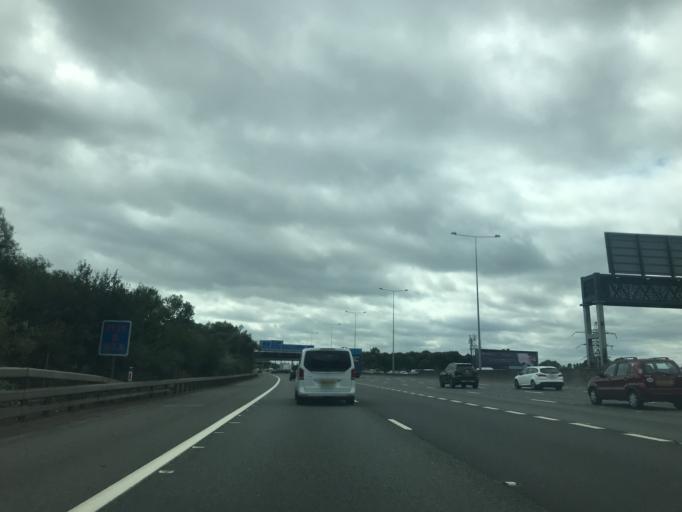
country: GB
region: England
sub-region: Buckinghamshire
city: Iver
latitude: 51.4819
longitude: -0.5018
